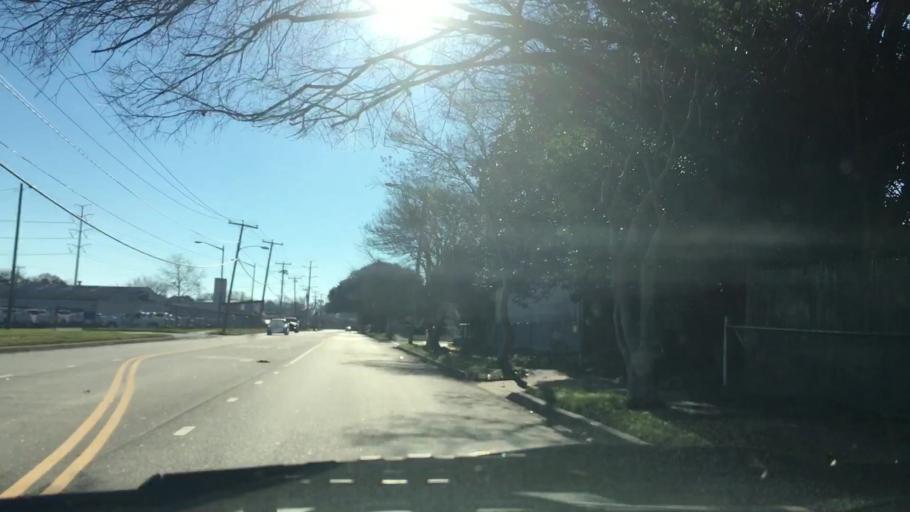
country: US
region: Virginia
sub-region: City of Norfolk
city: Norfolk
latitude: 36.8803
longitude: -76.2546
